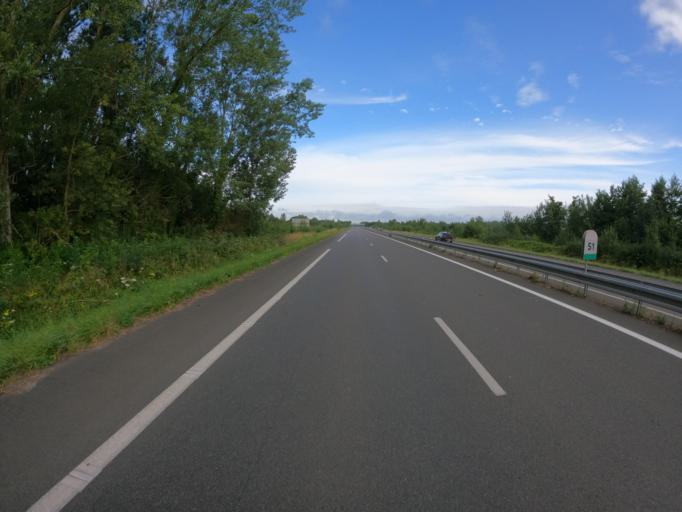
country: FR
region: Centre
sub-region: Departement d'Indre-et-Loire
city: Saint-Nicolas-de-Bourgueil
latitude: 47.2685
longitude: 0.1162
